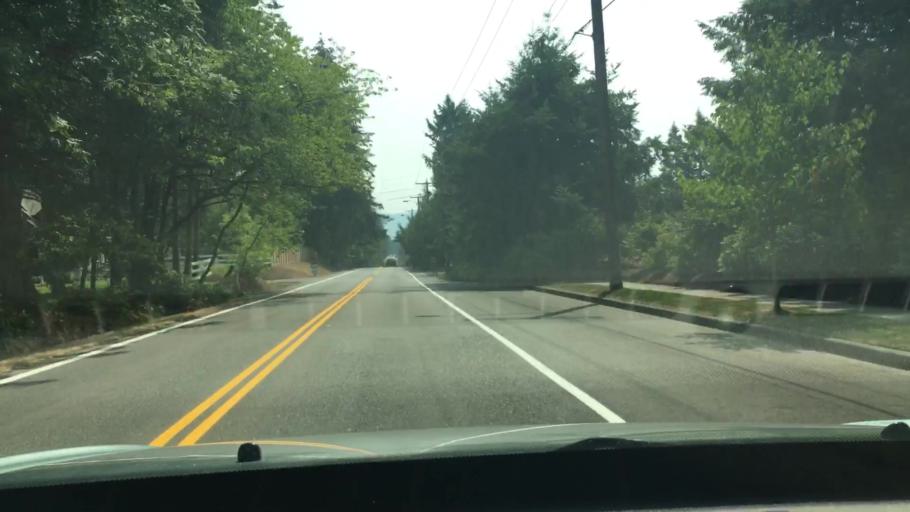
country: US
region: Washington
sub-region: King County
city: City of Sammamish
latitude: 47.6009
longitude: -122.0571
